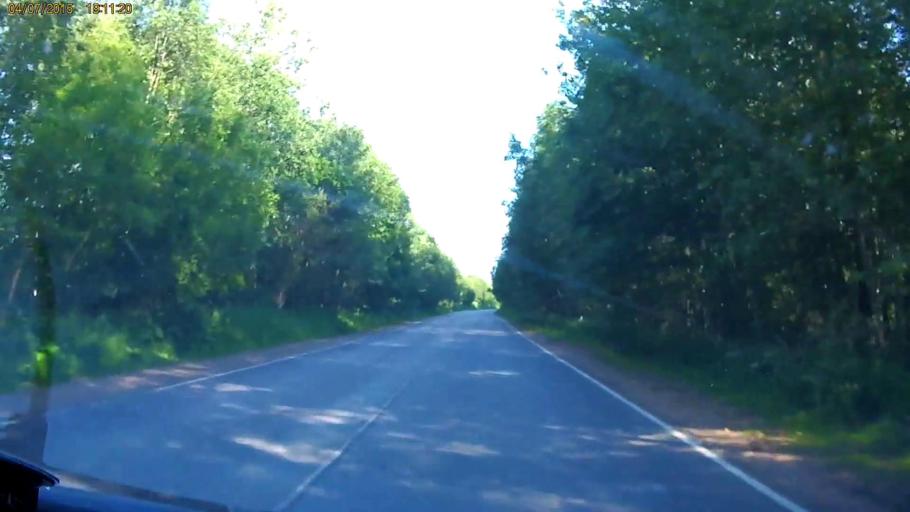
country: RU
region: Leningrad
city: Garbolovo
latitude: 60.3290
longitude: 30.4926
